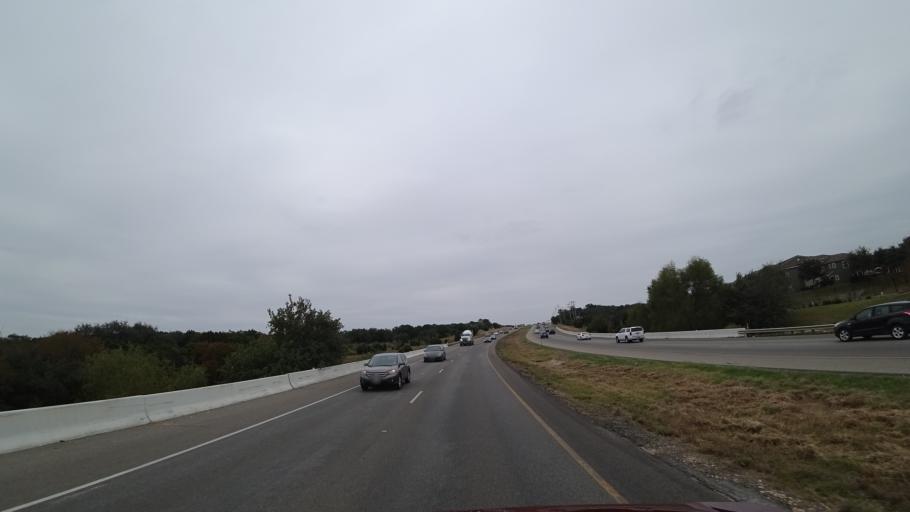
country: US
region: Texas
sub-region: Williamson County
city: Brushy Creek
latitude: 30.5297
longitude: -97.7784
